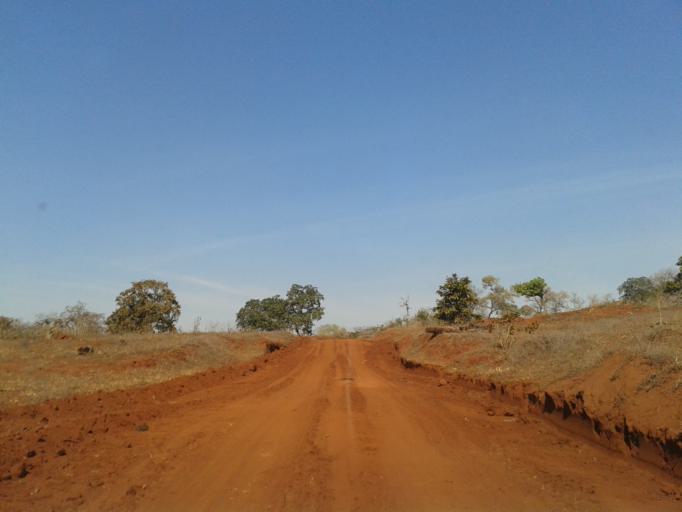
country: BR
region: Minas Gerais
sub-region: Santa Vitoria
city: Santa Vitoria
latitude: -19.2218
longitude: -50.0439
